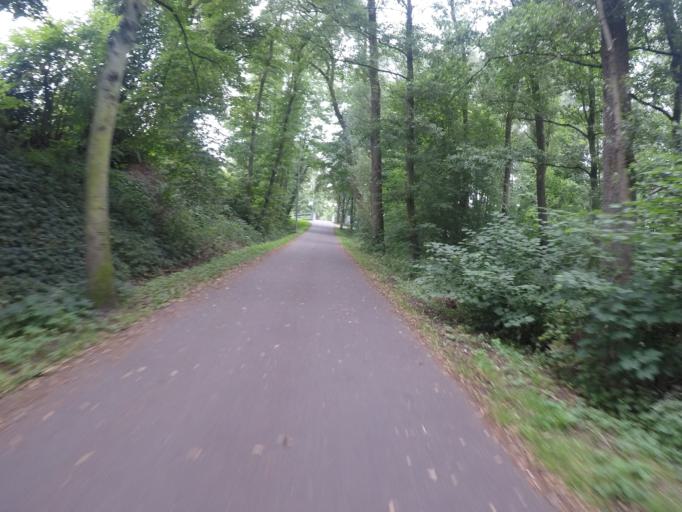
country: DE
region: Lower Saxony
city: Stade
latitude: 53.5977
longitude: 9.4662
